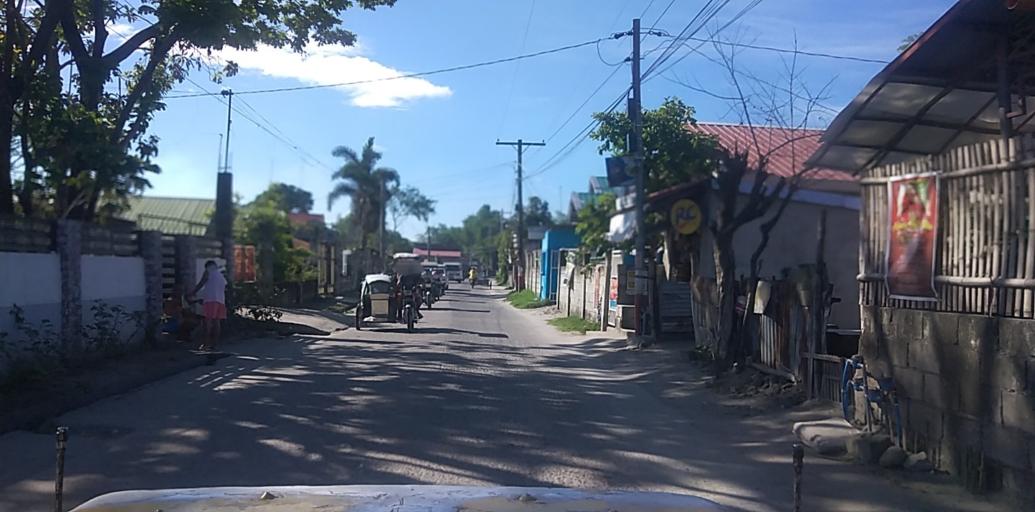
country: PH
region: Central Luzon
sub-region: Province of Pampanga
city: San Patricio
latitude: 15.0937
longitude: 120.7133
